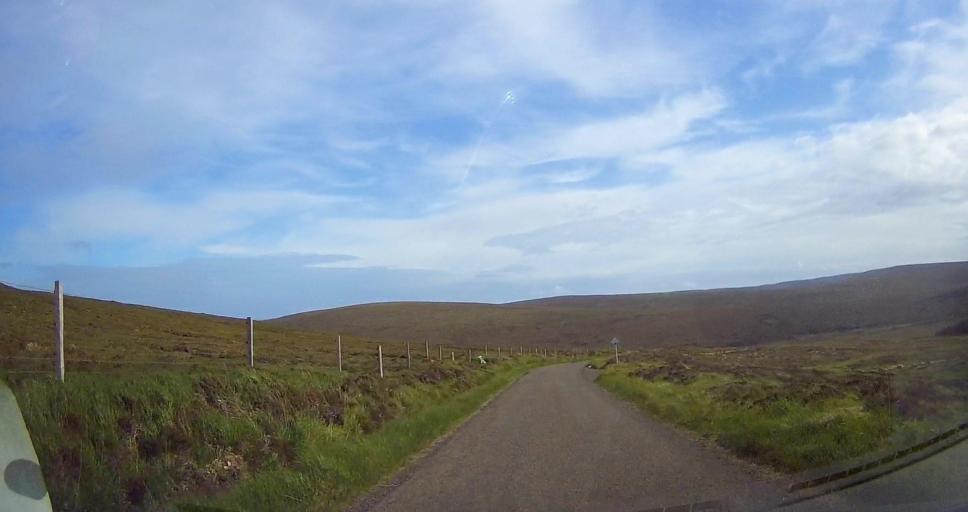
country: GB
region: Scotland
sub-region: Orkney Islands
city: Stromness
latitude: 58.8779
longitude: -3.2472
